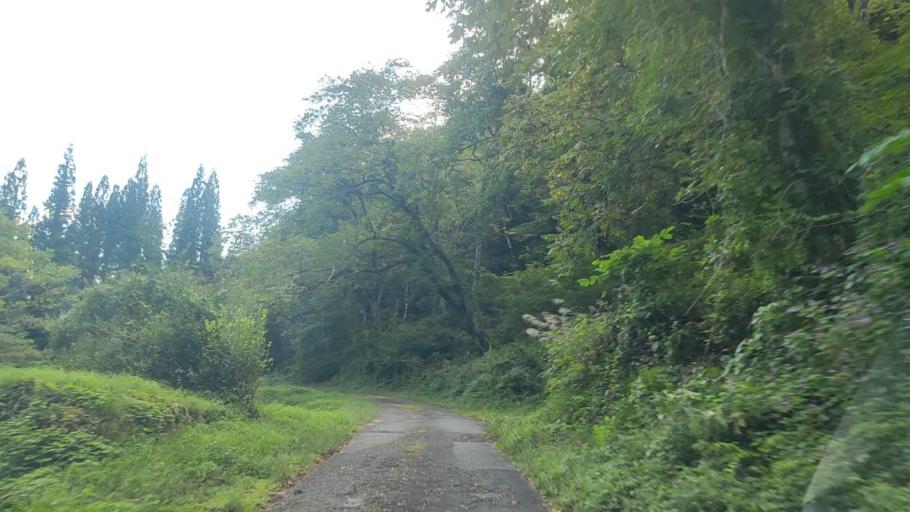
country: JP
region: Toyama
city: Yatsuomachi-higashikumisaka
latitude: 36.3241
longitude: 137.0810
